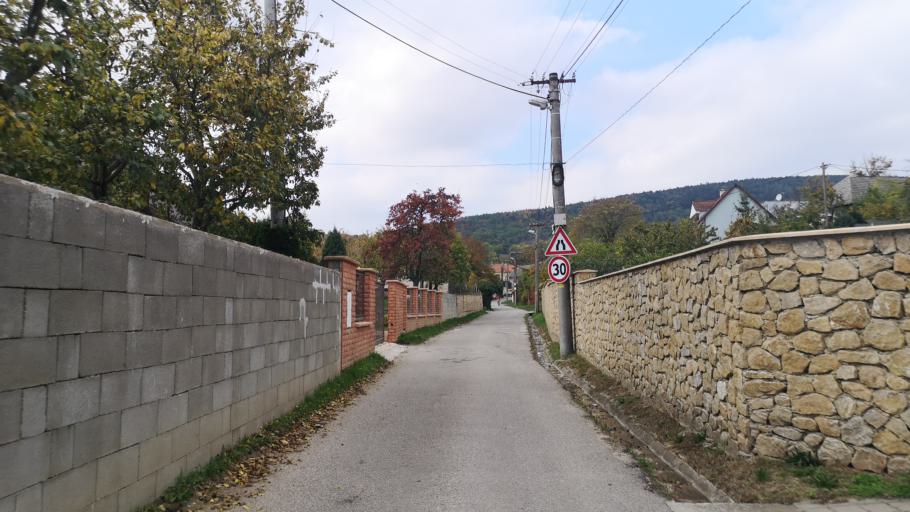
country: SK
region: Nitriansky
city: Cachtice
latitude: 48.7143
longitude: 17.7852
